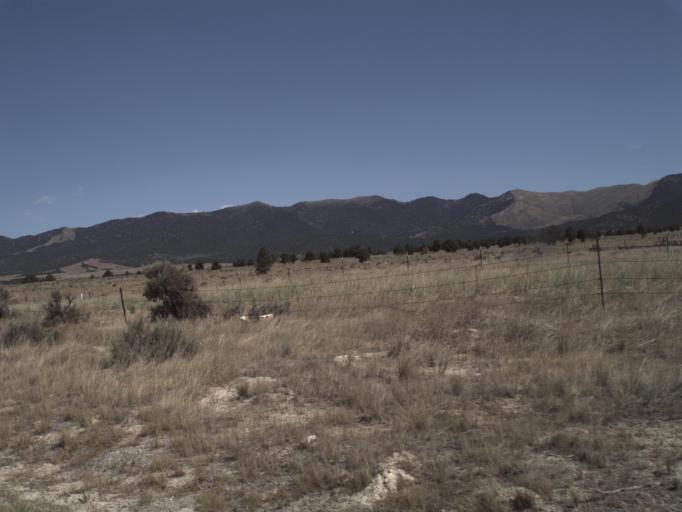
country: US
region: Utah
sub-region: Utah County
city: Genola
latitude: 39.9312
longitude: -112.1682
